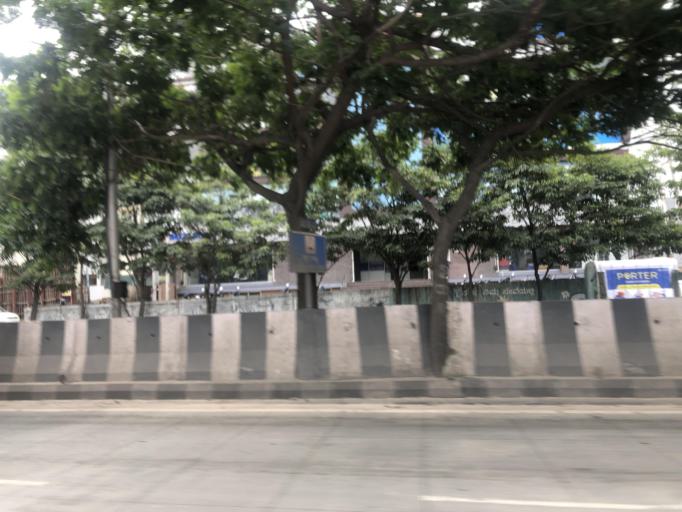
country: IN
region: Karnataka
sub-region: Bangalore Urban
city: Bangalore
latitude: 12.9585
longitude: 77.5177
